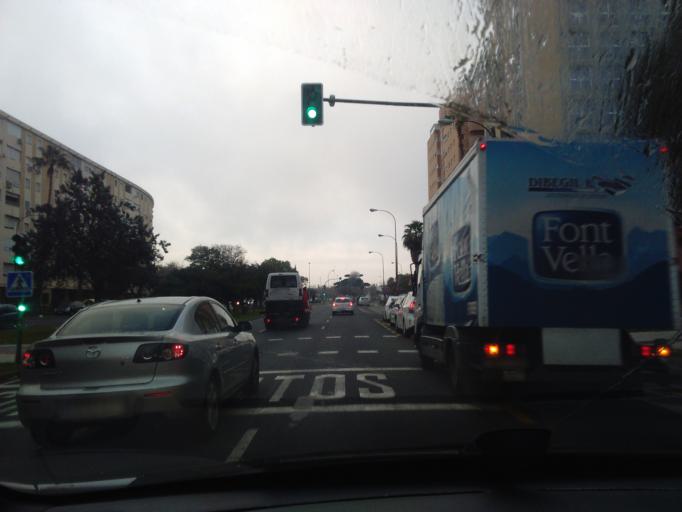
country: ES
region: Andalusia
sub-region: Provincia de Sevilla
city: Sevilla
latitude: 37.3888
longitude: -5.9204
